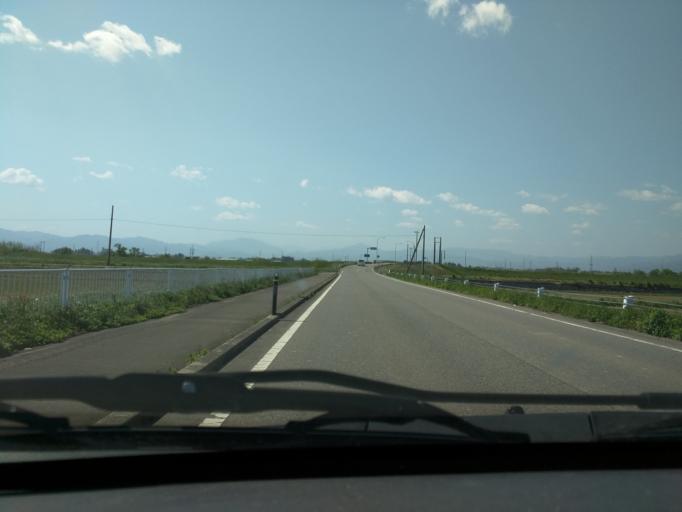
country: JP
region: Fukushima
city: Kitakata
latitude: 37.5902
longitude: 139.8701
